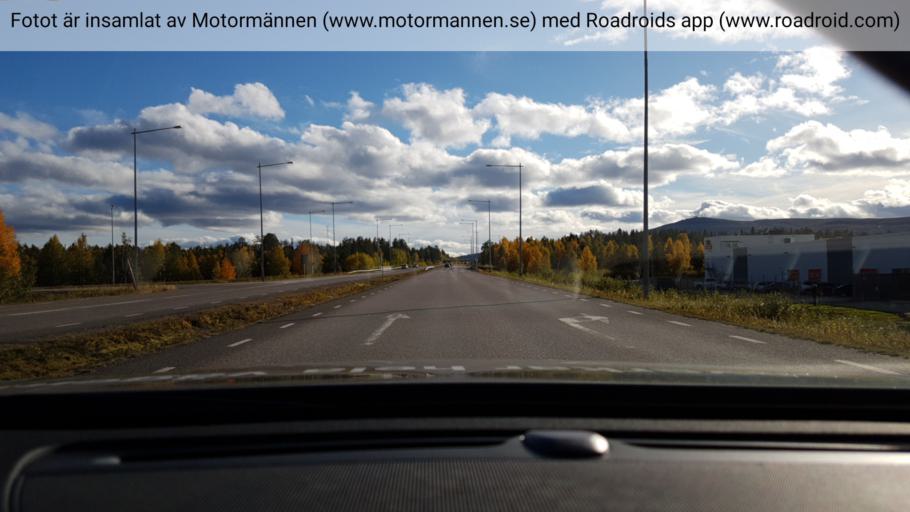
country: SE
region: Norrbotten
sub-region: Gallivare Kommun
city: Gaellivare
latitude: 67.1488
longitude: 20.6638
